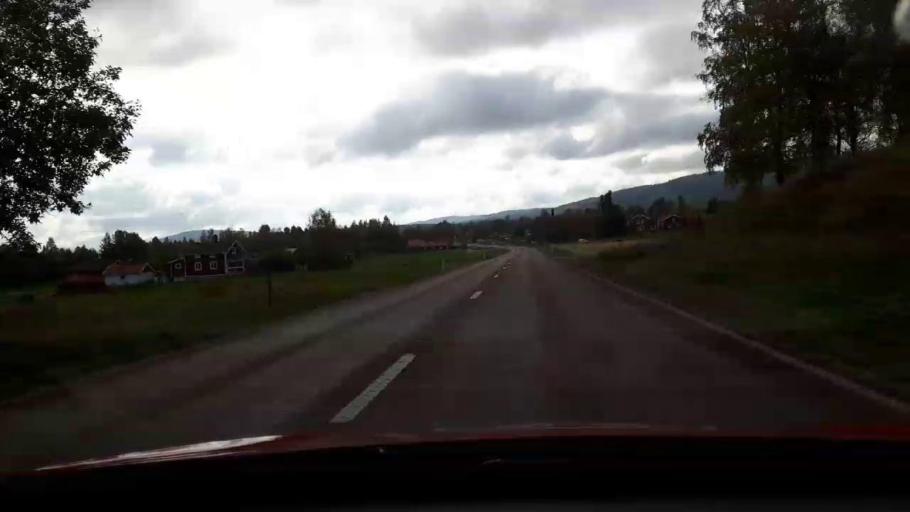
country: SE
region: Gaevleborg
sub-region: Ljusdals Kommun
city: Jaervsoe
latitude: 61.6770
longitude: 16.1451
